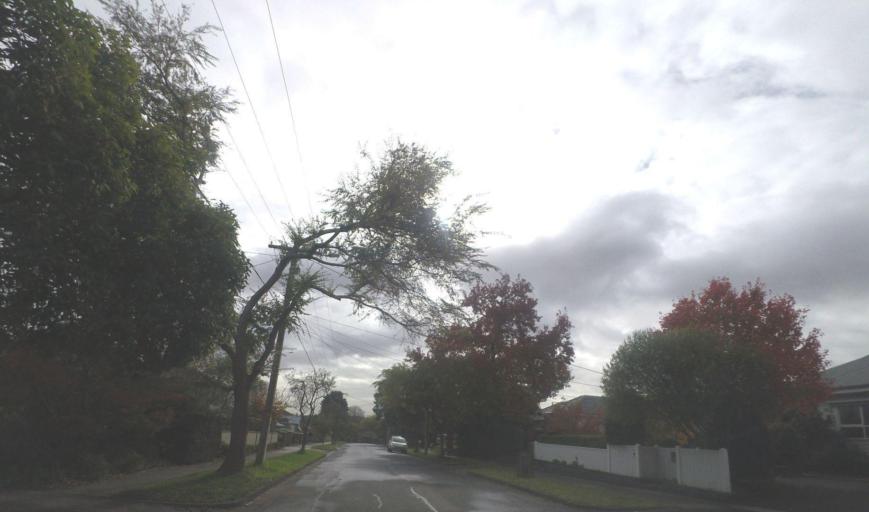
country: AU
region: Victoria
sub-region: Whitehorse
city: Nunawading
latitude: -37.8096
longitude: 145.1723
